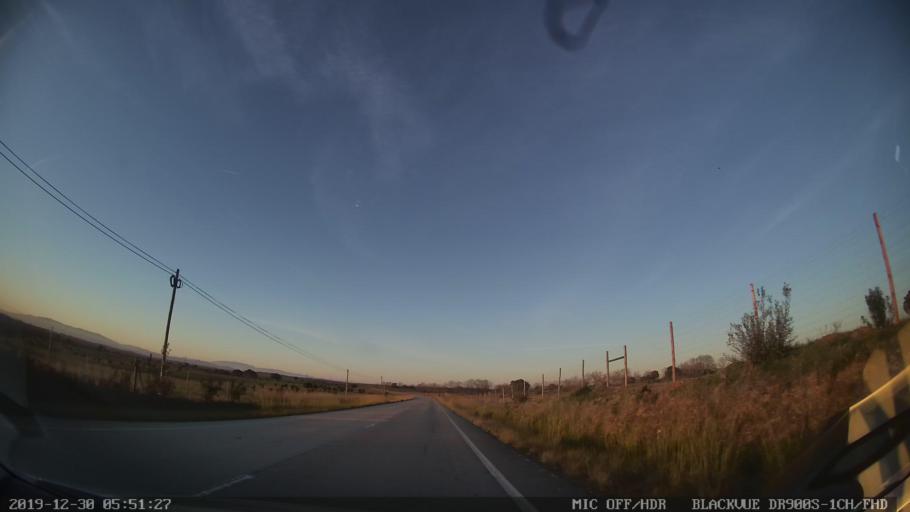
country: PT
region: Castelo Branco
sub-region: Idanha-A-Nova
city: Idanha-a-Nova
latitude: 39.9951
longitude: -7.2441
